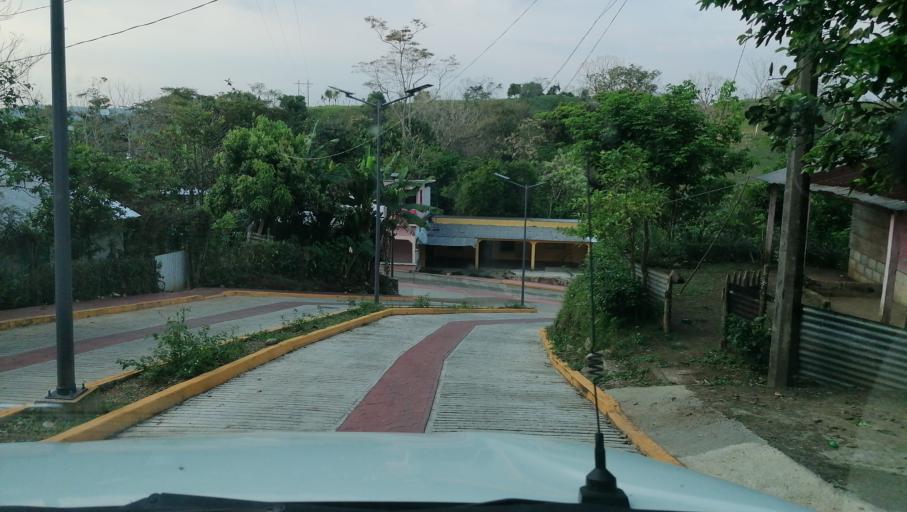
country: MX
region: Chiapas
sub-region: Juarez
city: El Triunfo 1ra. Seccion (Cardona)
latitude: 17.4941
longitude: -93.2435
